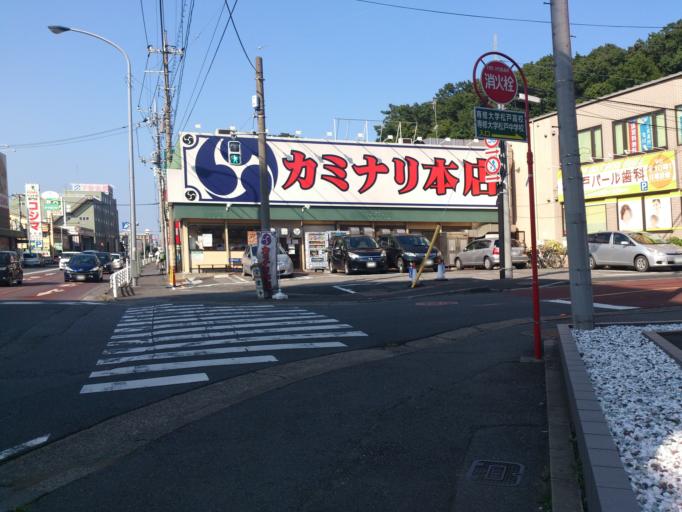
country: JP
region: Chiba
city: Matsudo
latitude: 35.8014
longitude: 139.9134
